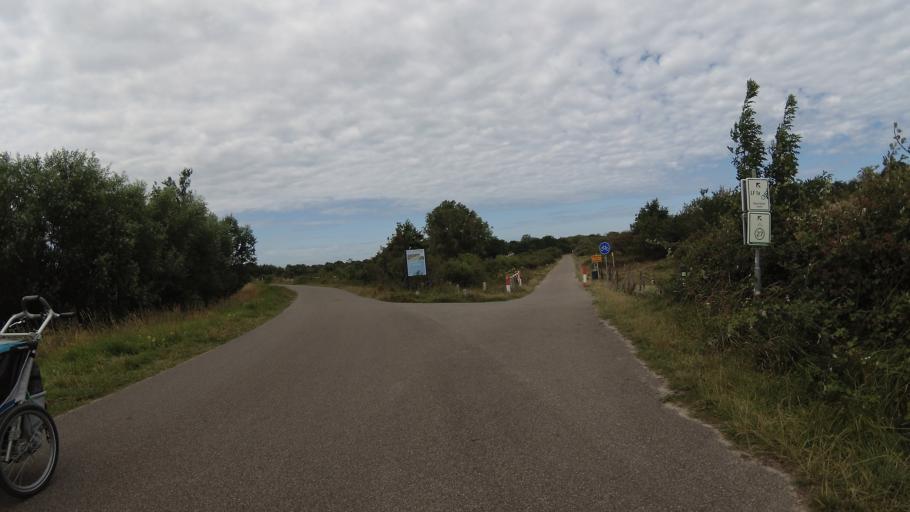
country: NL
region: Zeeland
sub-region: Gemeente Veere
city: Veere
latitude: 51.5877
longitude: 3.6107
